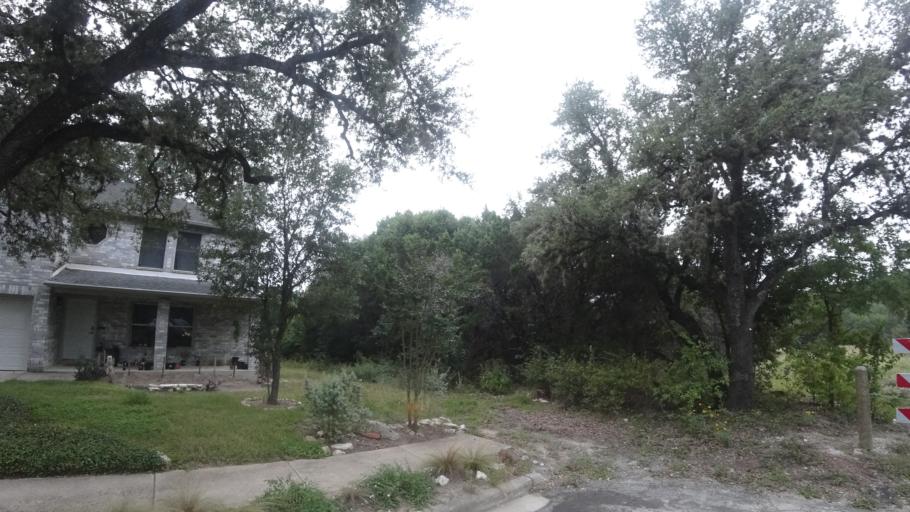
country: US
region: Texas
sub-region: Travis County
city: Wells Branch
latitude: 30.3657
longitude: -97.6706
